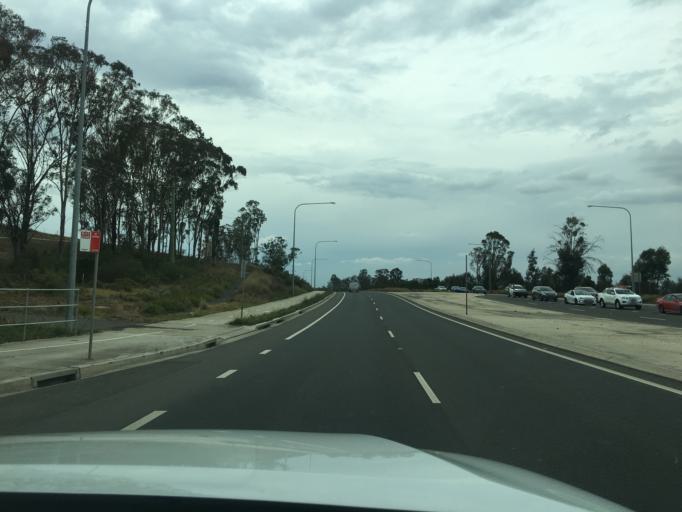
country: AU
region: New South Wales
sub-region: Campbelltown Municipality
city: Denham Court
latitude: -33.9754
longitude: 150.8099
